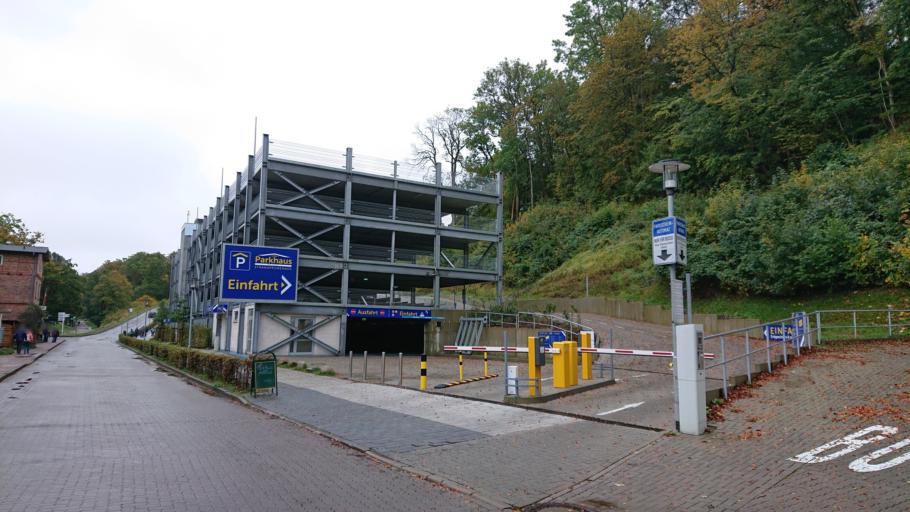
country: DE
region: Mecklenburg-Vorpommern
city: Ostseebad Gohren
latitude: 54.3457
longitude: 13.7381
